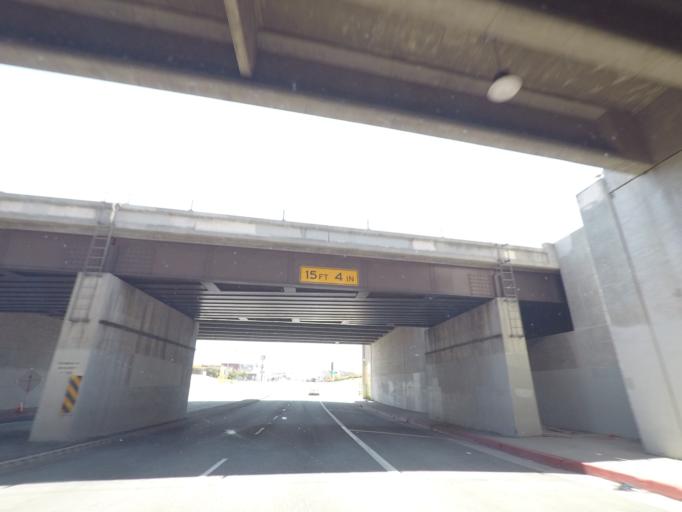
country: US
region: California
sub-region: Los Angeles County
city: East Pasadena
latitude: 34.1494
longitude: -118.0736
